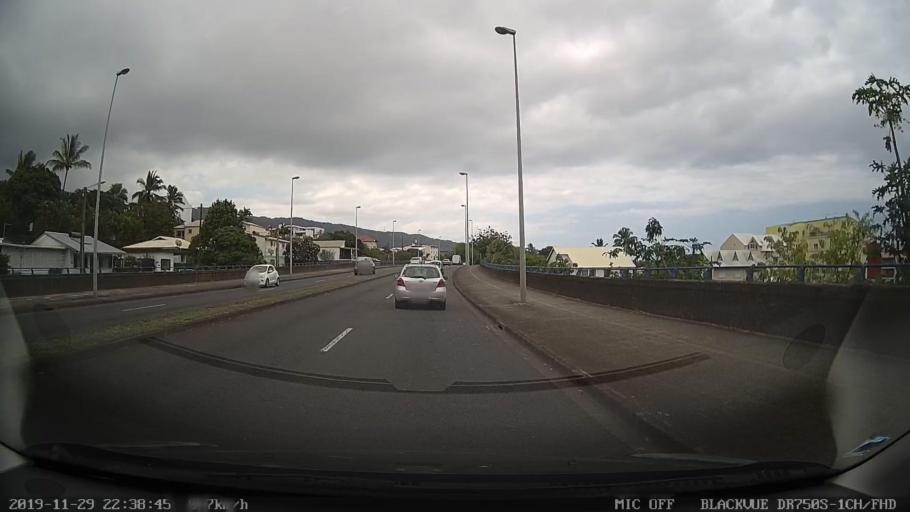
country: RE
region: Reunion
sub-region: Reunion
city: Saint-Denis
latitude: -20.8989
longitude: 55.4781
